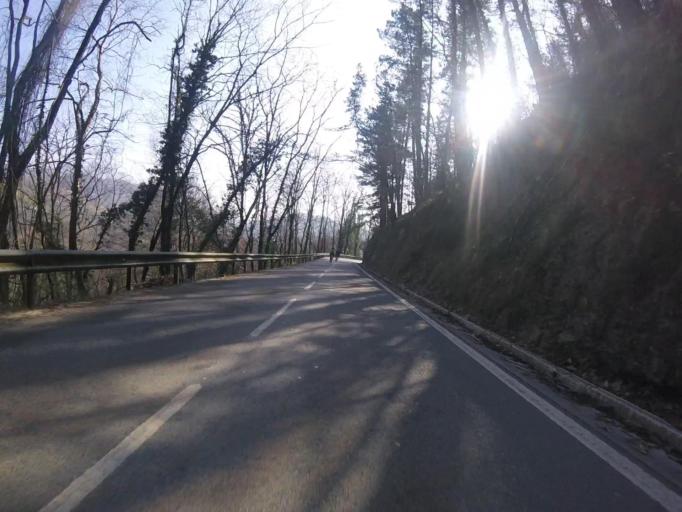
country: ES
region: Navarre
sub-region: Provincia de Navarra
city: Bera
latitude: 43.2926
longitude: -1.6895
